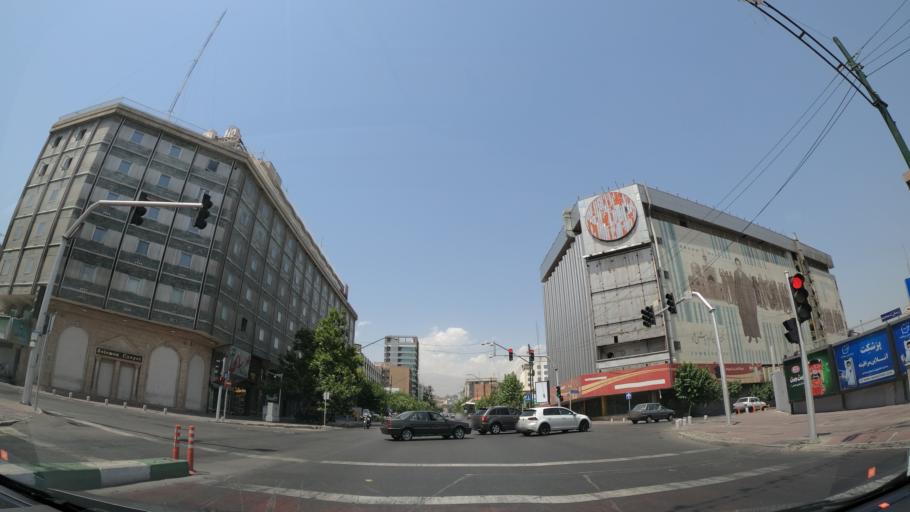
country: IR
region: Tehran
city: Tehran
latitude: 35.7215
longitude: 51.4137
